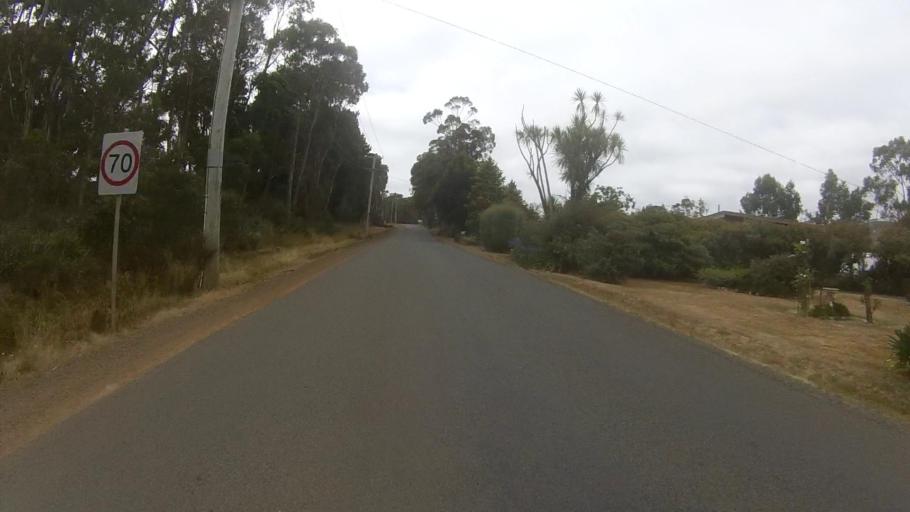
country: AU
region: Tasmania
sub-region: Kingborough
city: Kingston
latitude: -42.9650
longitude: 147.2368
